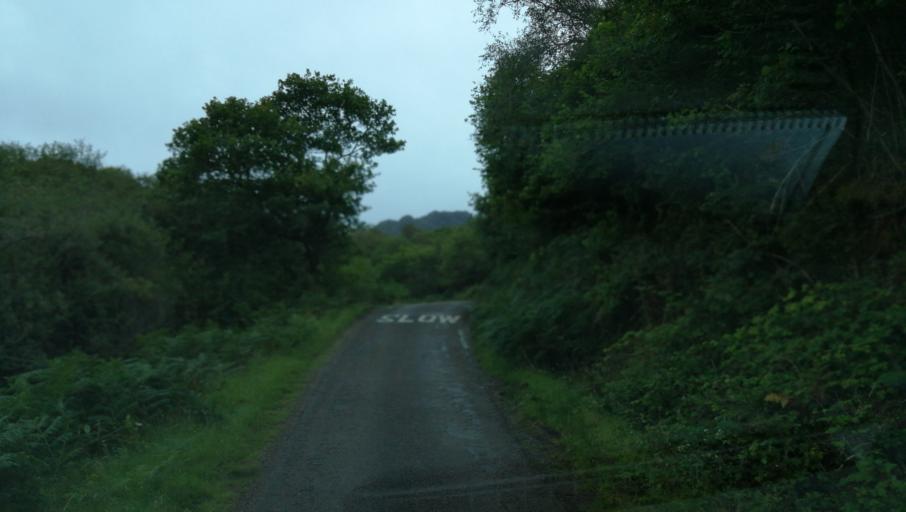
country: GB
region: Scotland
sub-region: Argyll and Bute
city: Isle Of Mull
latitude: 56.7196
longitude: -6.1686
